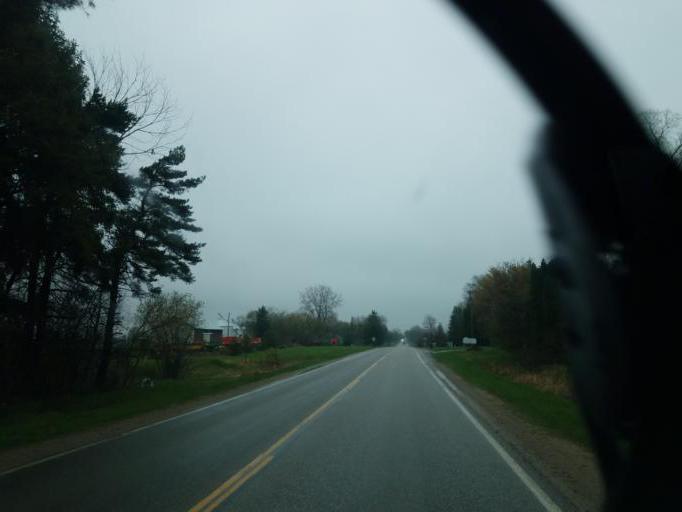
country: US
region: Michigan
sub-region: Isabella County
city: Shepherd
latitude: 43.5241
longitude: -84.7639
